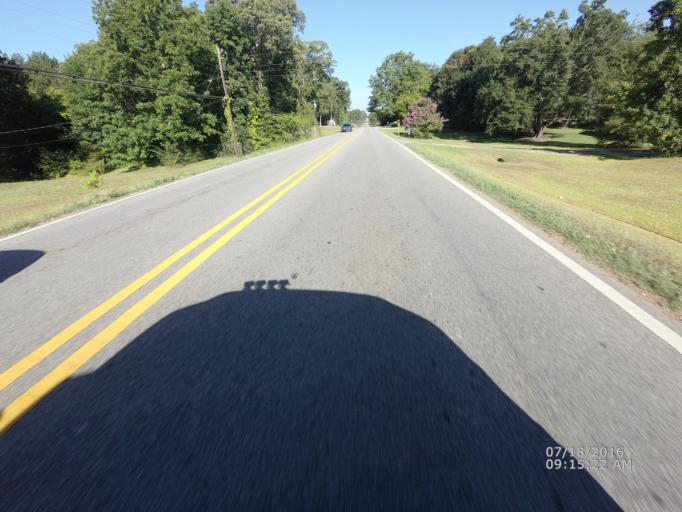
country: US
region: Alabama
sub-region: Chambers County
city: Huguley
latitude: 32.8487
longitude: -85.2523
